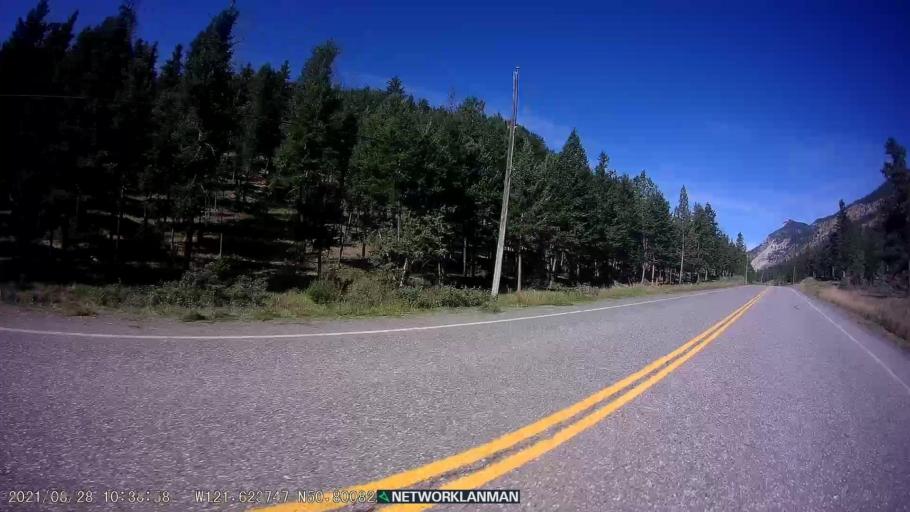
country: CA
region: British Columbia
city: Cache Creek
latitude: 50.8007
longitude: -121.6228
